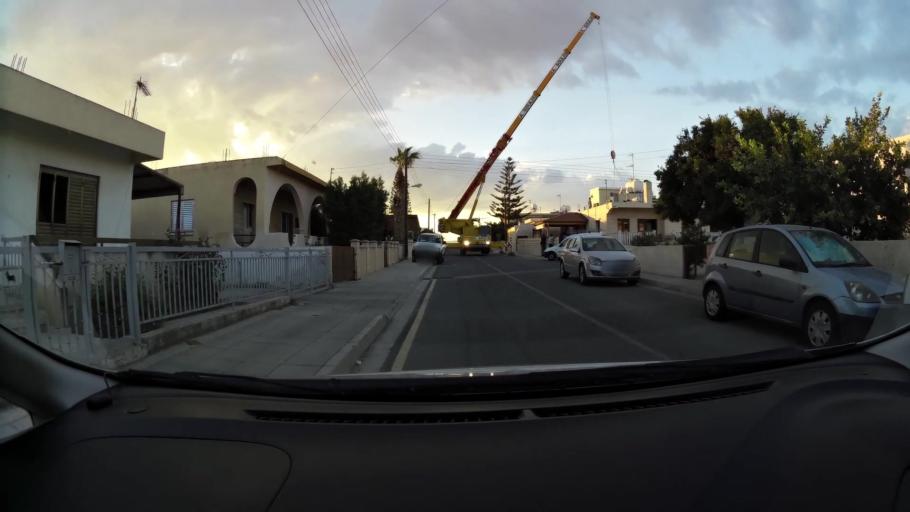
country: CY
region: Larnaka
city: Dhromolaxia
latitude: 34.8667
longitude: 33.5858
